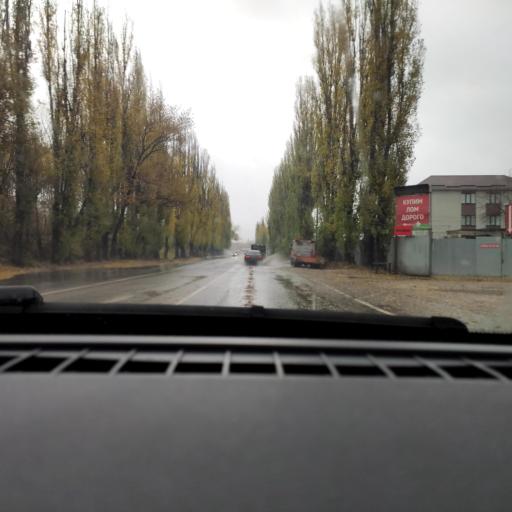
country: RU
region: Voronezj
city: Maslovka
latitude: 51.6234
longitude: 39.2421
